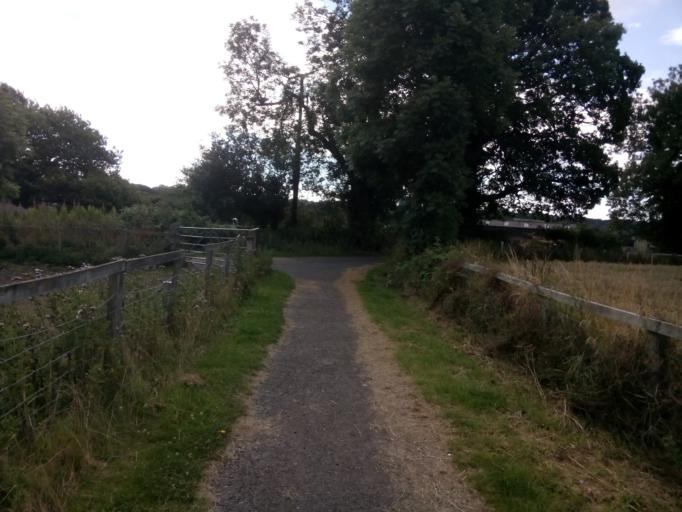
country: GB
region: England
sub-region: County Durham
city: Durham
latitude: 54.7938
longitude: -1.5621
